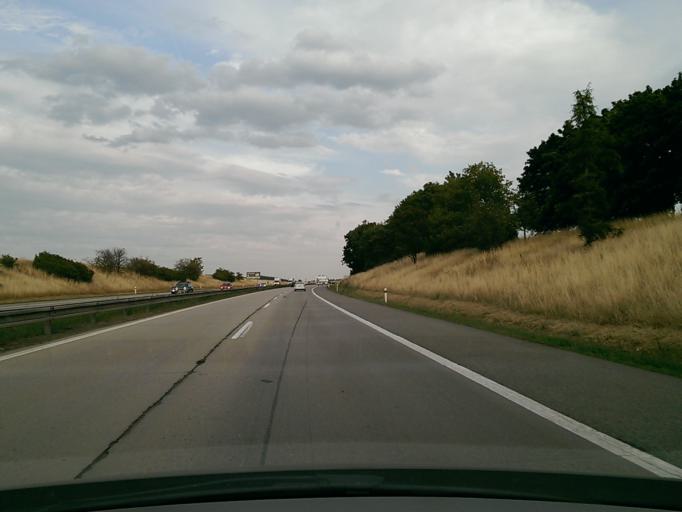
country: CZ
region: Vysocina
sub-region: Okres Zd'ar nad Sazavou
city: Velke Mezirici
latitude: 49.3314
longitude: 16.0705
